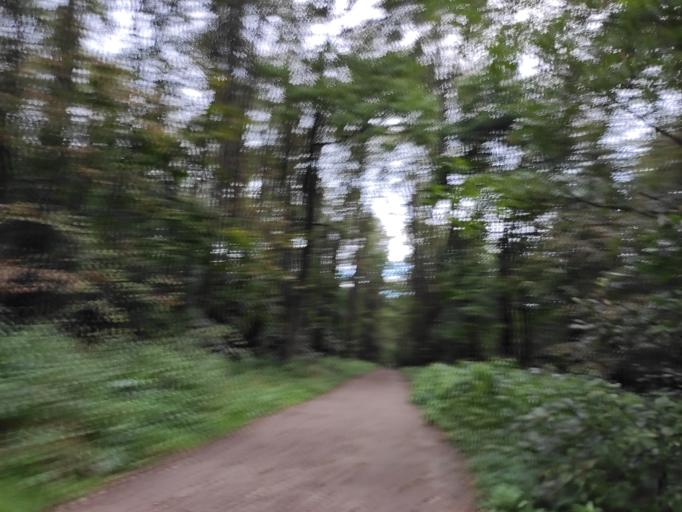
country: RU
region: Moskovskaya
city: Izmaylovo
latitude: 55.7707
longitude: 37.7894
